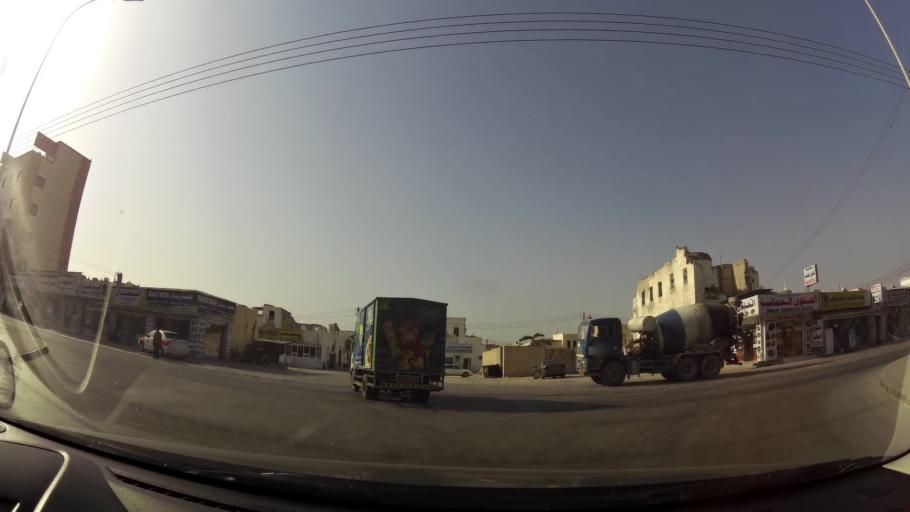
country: OM
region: Zufar
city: Salalah
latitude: 17.0092
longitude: 54.0980
